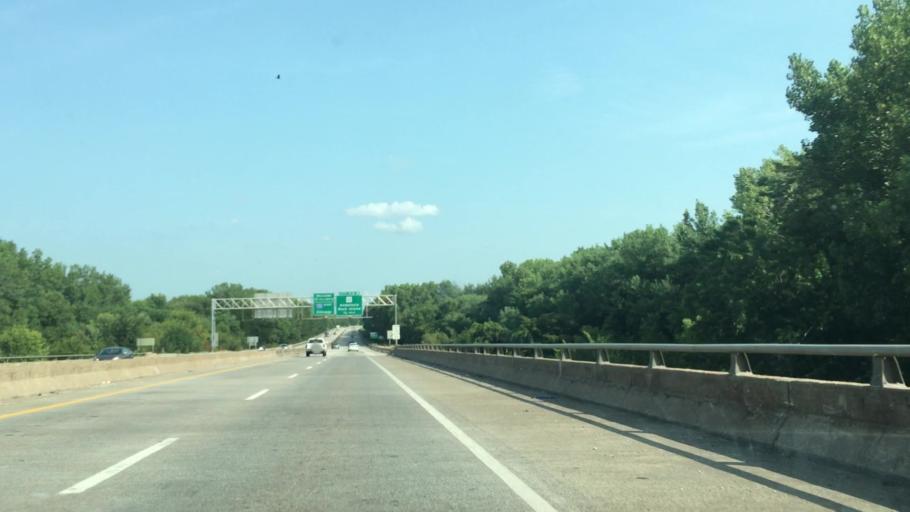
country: US
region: Illinois
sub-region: Rock Island County
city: Rock Island
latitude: 41.4753
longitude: -90.6276
